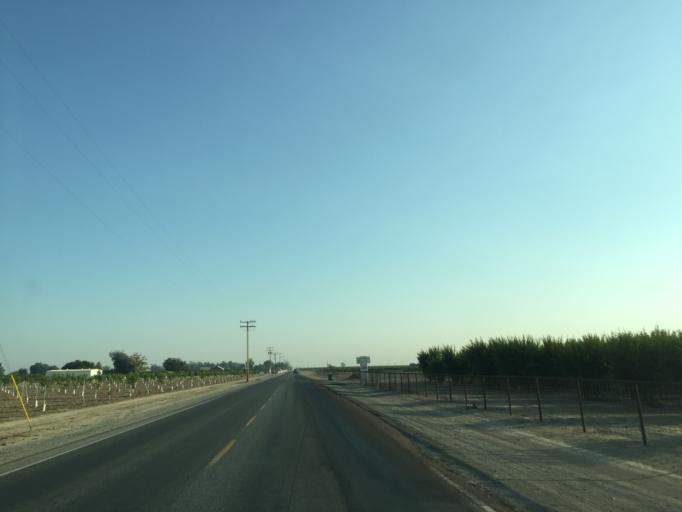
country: US
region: California
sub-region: Tulare County
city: Ivanhoe
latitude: 36.4148
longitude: -119.2782
